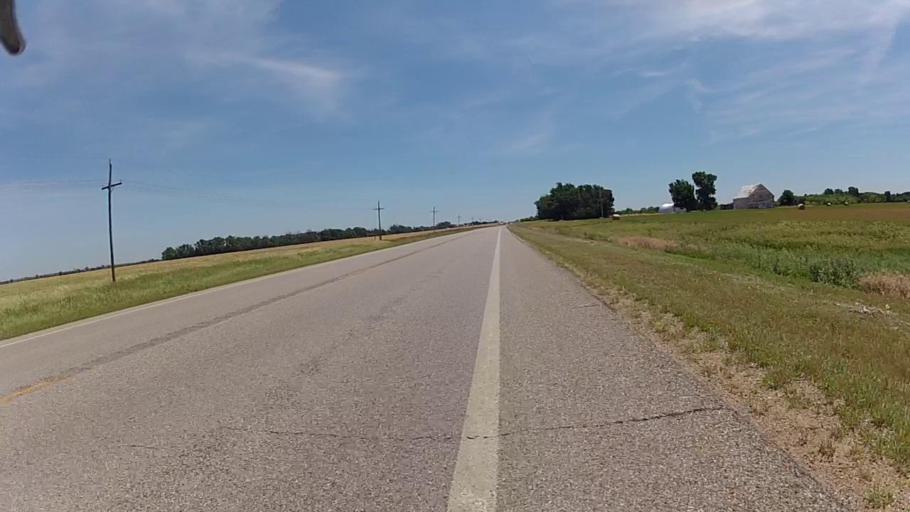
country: US
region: Kansas
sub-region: Barber County
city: Medicine Lodge
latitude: 37.2540
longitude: -98.4923
